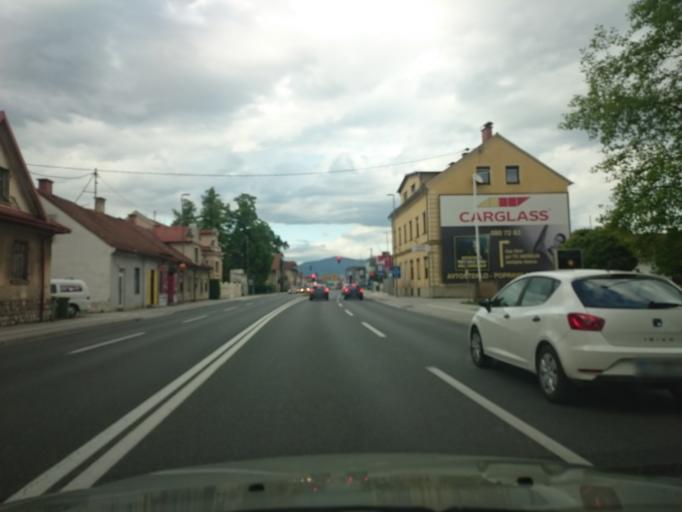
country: SI
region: Celje
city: Celje
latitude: 46.2383
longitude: 15.2733
